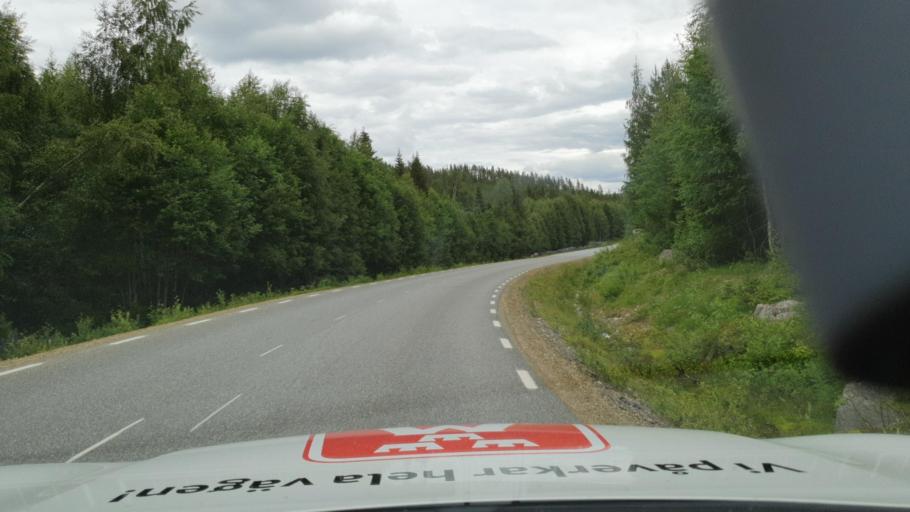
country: SE
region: Vaesterbotten
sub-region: Bjurholms Kommun
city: Bjurholm
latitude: 63.8807
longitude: 18.9953
